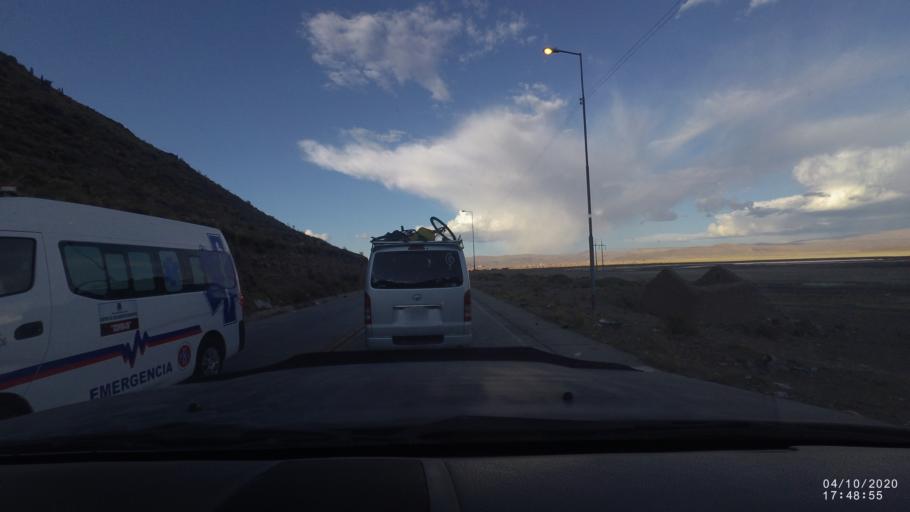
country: BO
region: Oruro
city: Oruro
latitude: -18.0141
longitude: -67.1384
